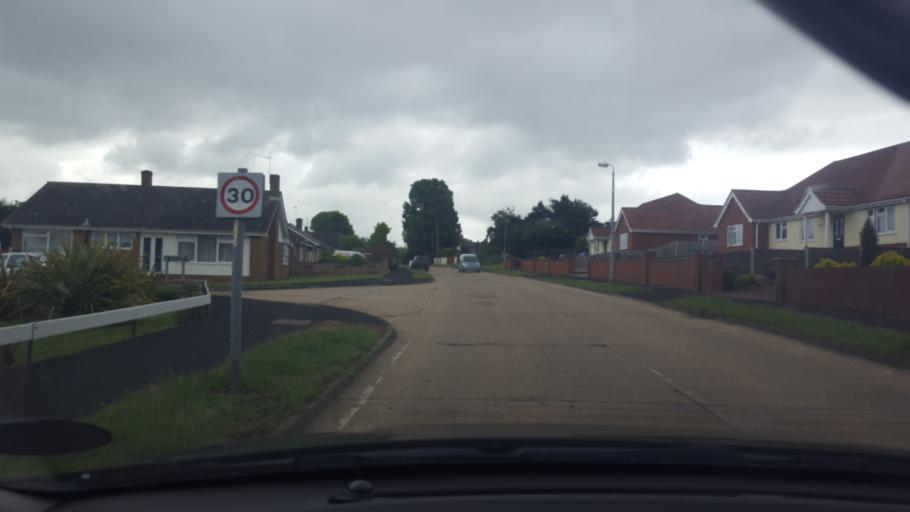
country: GB
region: England
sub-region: Essex
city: Brightlingsea
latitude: 51.7943
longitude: 1.0337
